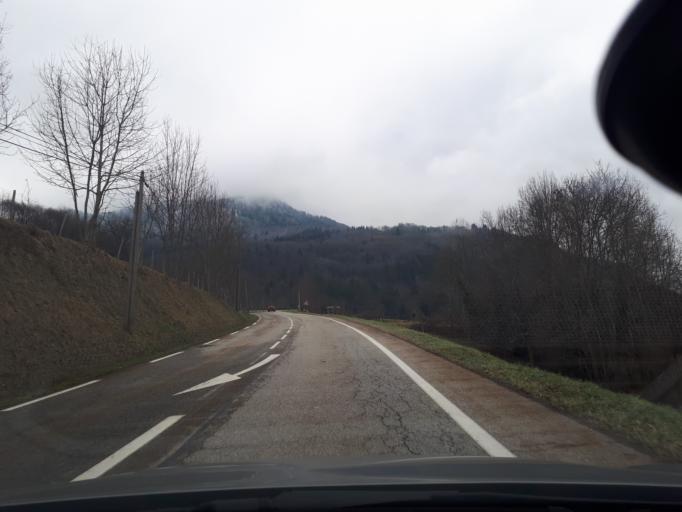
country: FR
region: Rhone-Alpes
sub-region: Departement de l'Isere
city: Vaulnaveys-le-Bas
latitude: 45.1148
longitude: 5.8287
